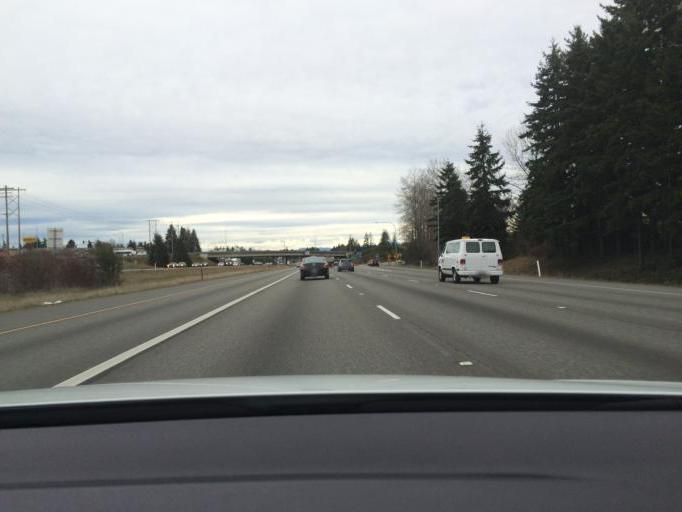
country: US
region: Washington
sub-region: Snohomish County
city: Martha Lake
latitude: 47.8792
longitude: -122.2368
